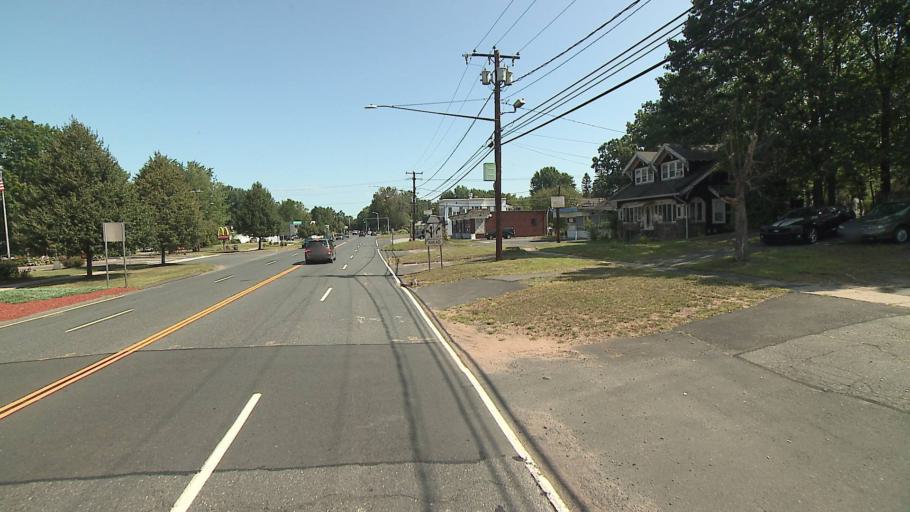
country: US
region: Connecticut
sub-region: Hartford County
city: Sherwood Manor
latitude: 42.0237
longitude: -72.5849
